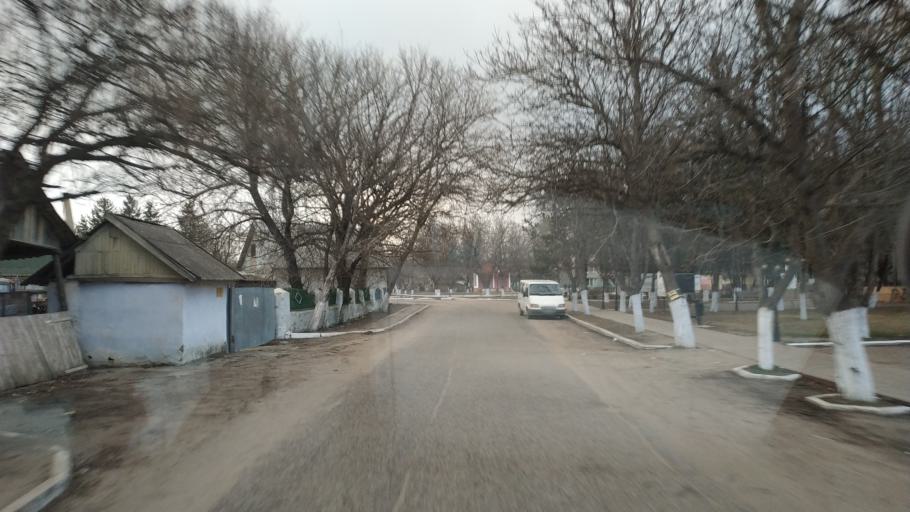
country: MD
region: Telenesti
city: Grigoriopol
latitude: 47.0901
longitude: 29.3486
